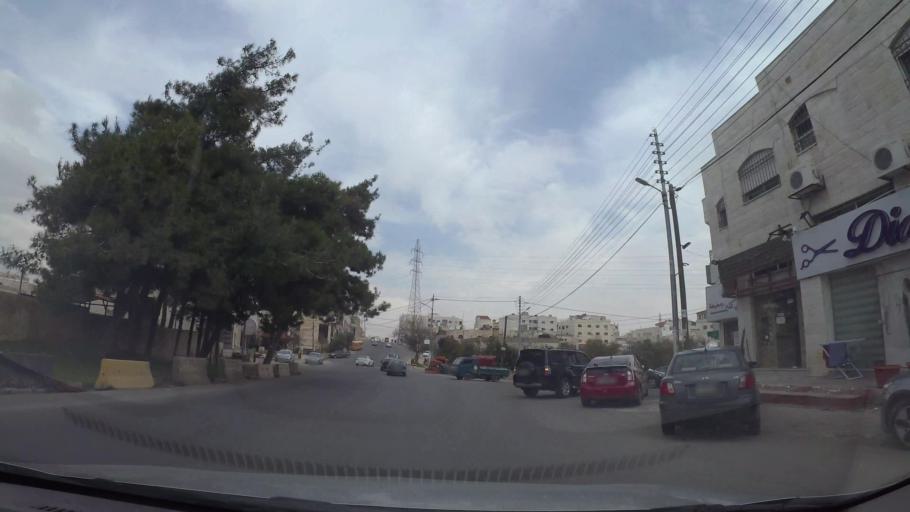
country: JO
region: Amman
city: Umm as Summaq
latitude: 31.8944
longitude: 35.8633
